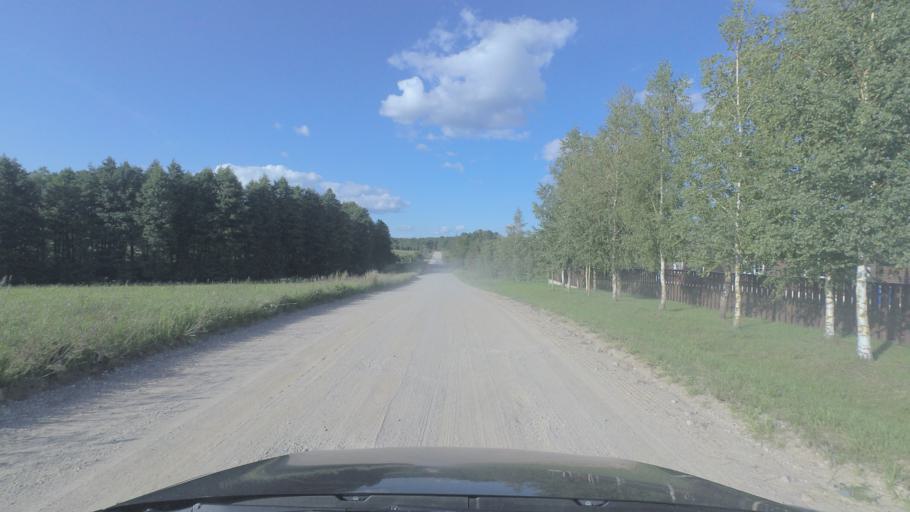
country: LT
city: Pabrade
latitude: 55.1365
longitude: 25.7095
